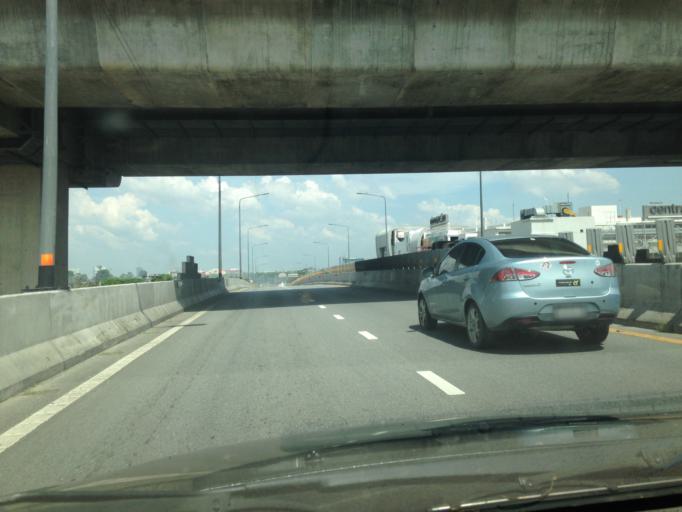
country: TH
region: Nonthaburi
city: Mueang Nonthaburi
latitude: 13.8656
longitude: 100.4939
